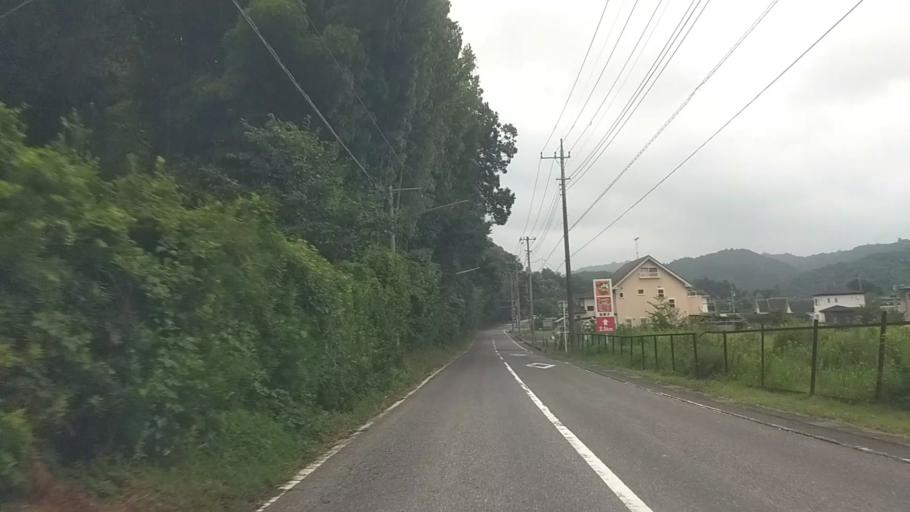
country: JP
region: Chiba
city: Kimitsu
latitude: 35.2343
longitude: 140.0043
